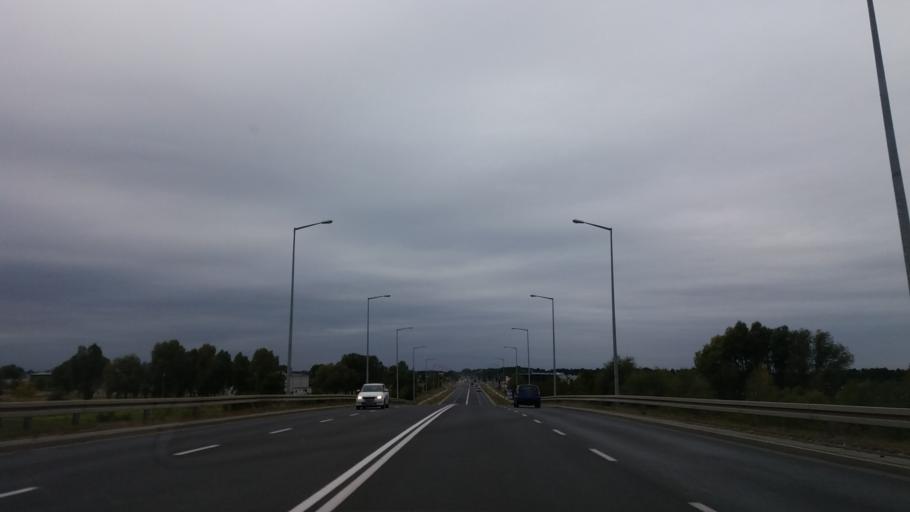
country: PL
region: Lubusz
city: Gorzow Wielkopolski
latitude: 52.7148
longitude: 15.2459
